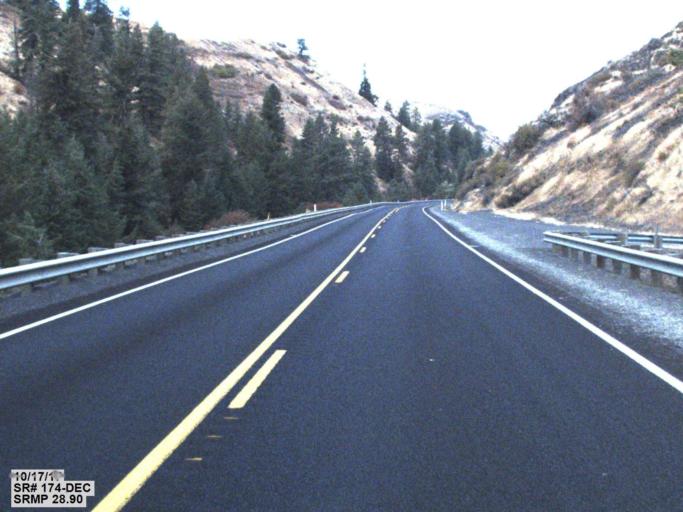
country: US
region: Washington
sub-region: Okanogan County
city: Coulee Dam
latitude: 47.9053
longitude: -118.8728
